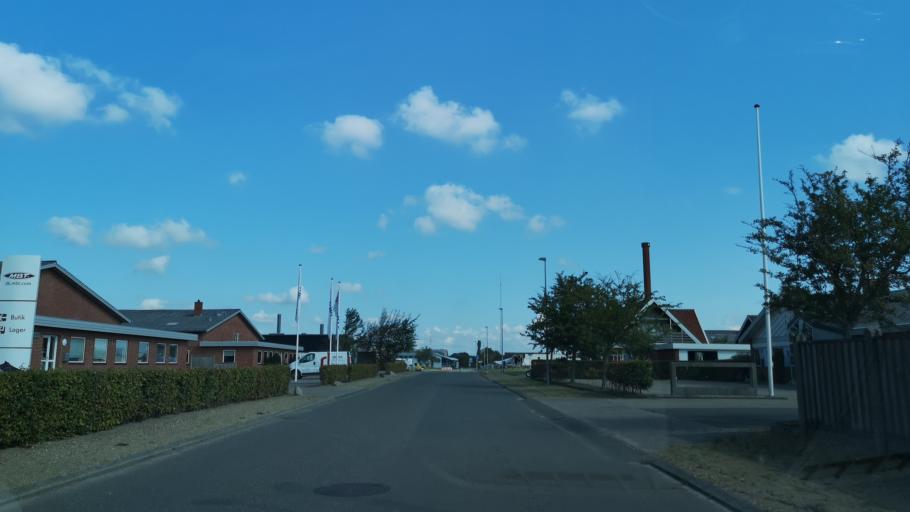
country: DK
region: Central Jutland
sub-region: Ringkobing-Skjern Kommune
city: Skjern
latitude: 55.9578
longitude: 8.4919
